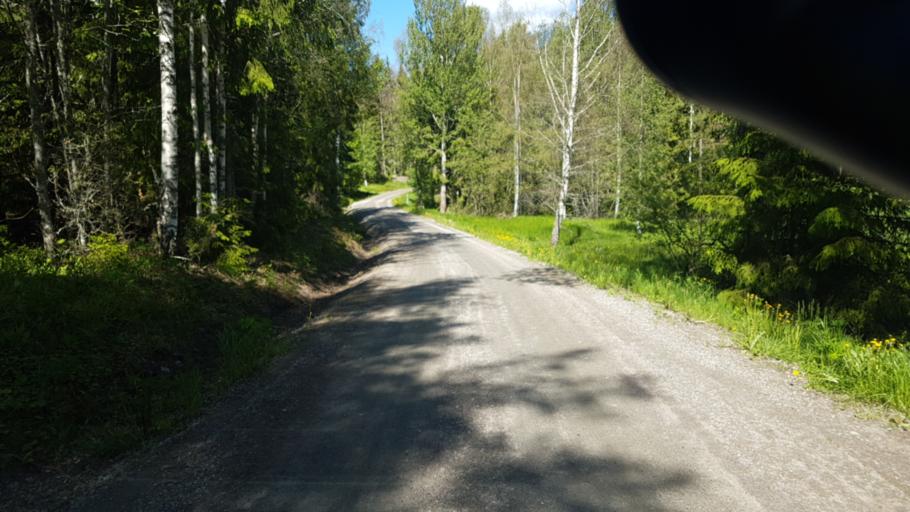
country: SE
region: Vaermland
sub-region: Arvika Kommun
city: Arvika
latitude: 59.5748
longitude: 12.8301
